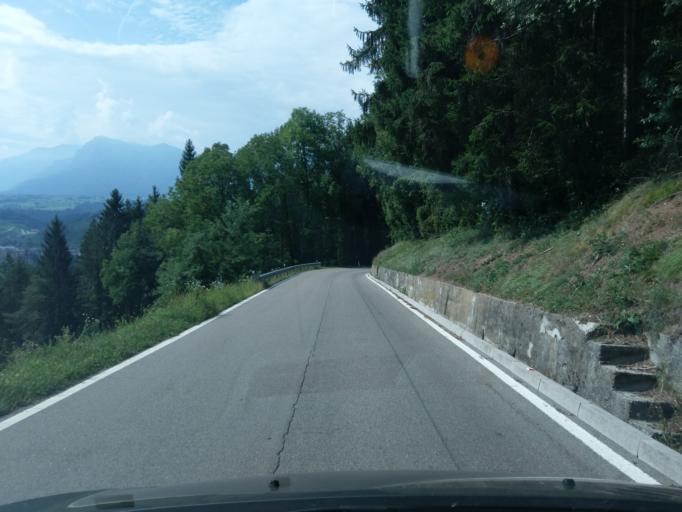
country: IT
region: Trentino-Alto Adige
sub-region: Provincia di Trento
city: Ponte Arche
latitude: 46.0452
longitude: 10.8817
